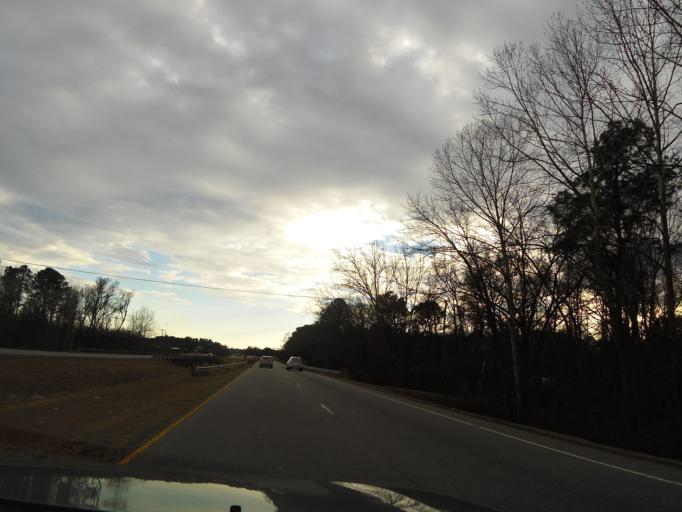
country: US
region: North Carolina
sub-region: Nash County
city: Rocky Mount
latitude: 35.9269
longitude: -77.8309
